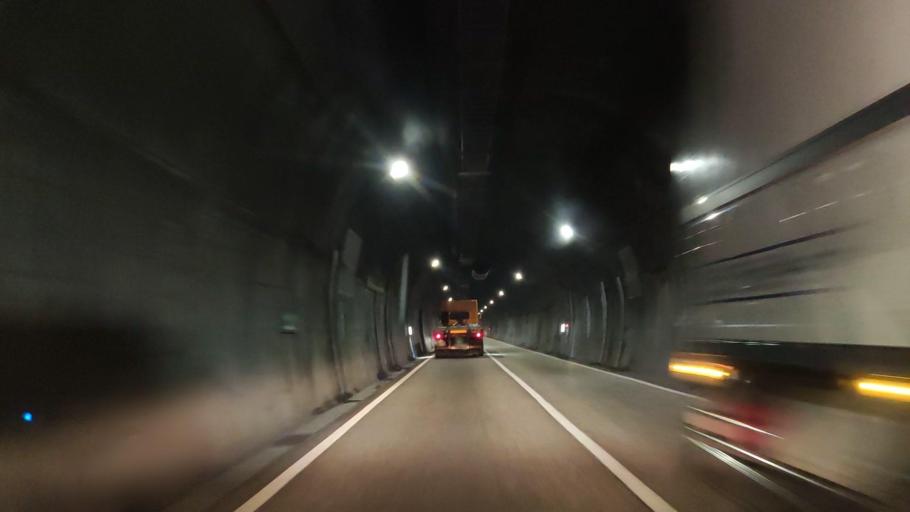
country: JP
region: Toyama
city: Nyuzen
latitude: 36.9674
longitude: 137.5824
